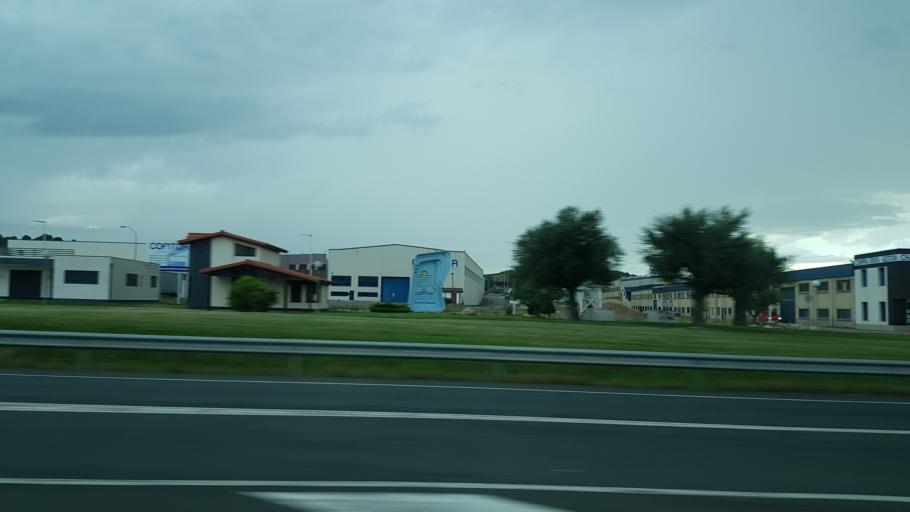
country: ES
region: La Rioja
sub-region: Provincia de La Rioja
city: Albelda de Iregua
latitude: 42.3910
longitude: -2.4756
